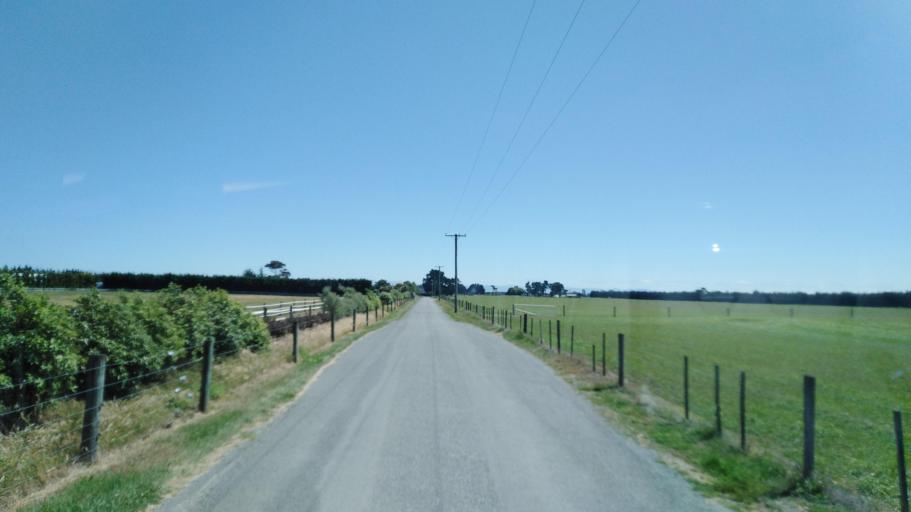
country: NZ
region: Canterbury
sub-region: Selwyn District
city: Rolleston
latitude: -43.5652
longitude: 172.4392
